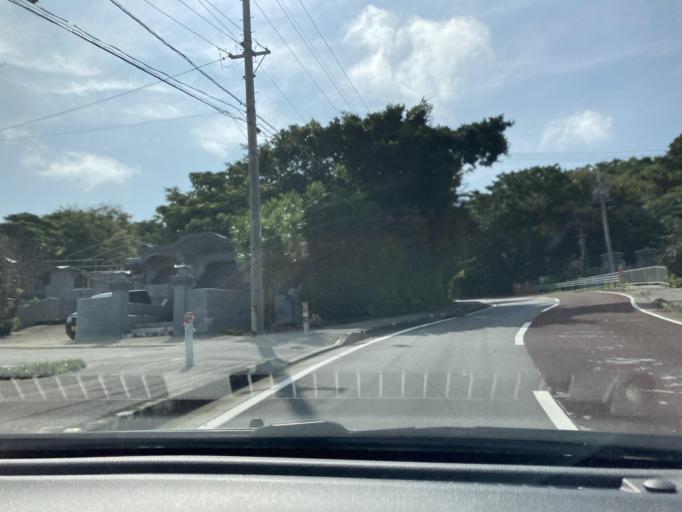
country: JP
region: Okinawa
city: Chatan
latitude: 26.2946
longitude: 127.7953
